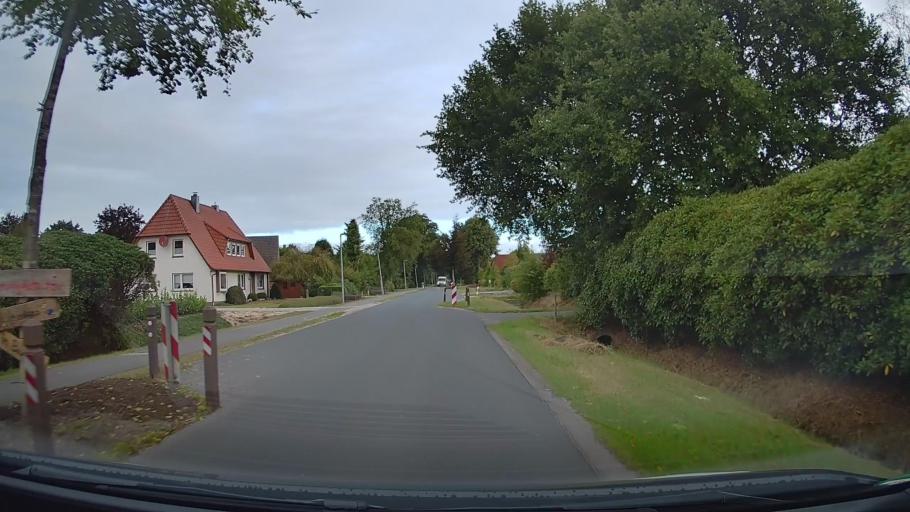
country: DE
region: Lower Saxony
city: Wardenburg
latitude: 53.1131
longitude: 8.1111
